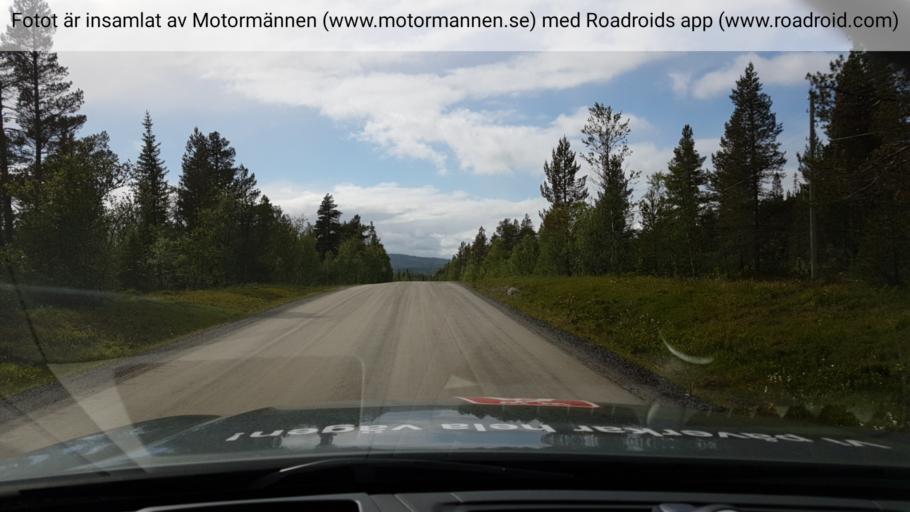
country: NO
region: Nord-Trondelag
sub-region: Snasa
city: Snaase
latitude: 63.7340
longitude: 12.5105
